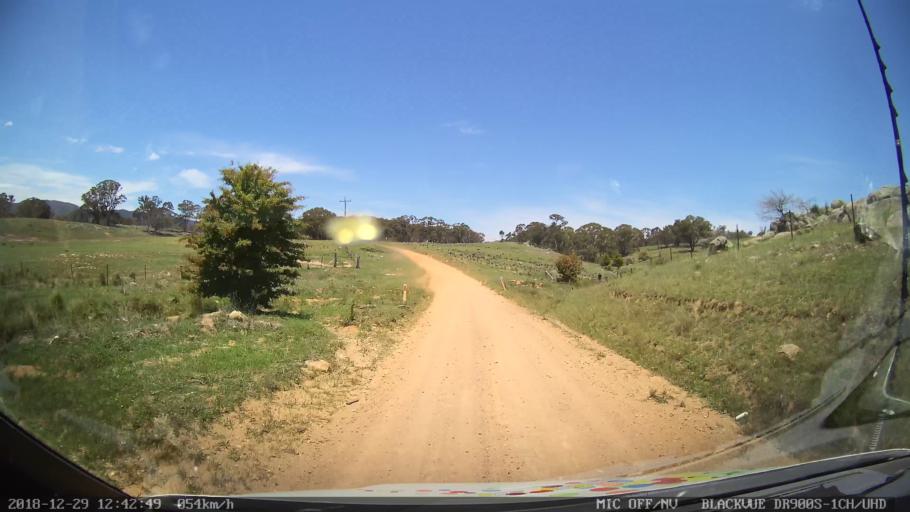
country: AU
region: Australian Capital Territory
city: Macarthur
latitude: -35.6158
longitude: 149.2186
